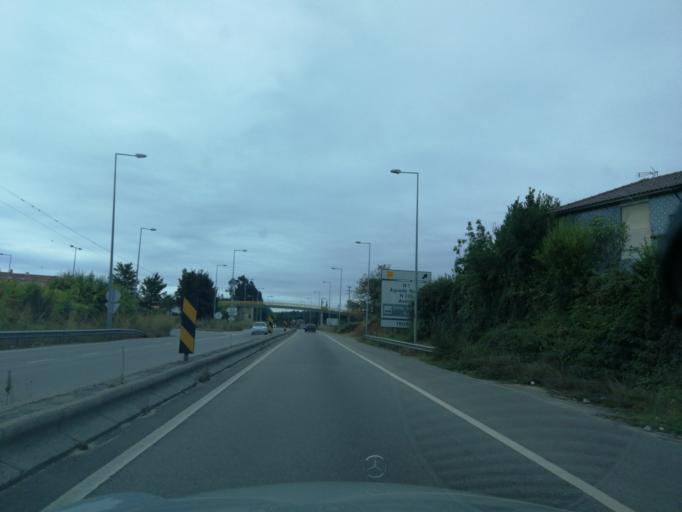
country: PT
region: Aveiro
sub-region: Agueda
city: Valongo
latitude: 40.6097
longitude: -8.4659
